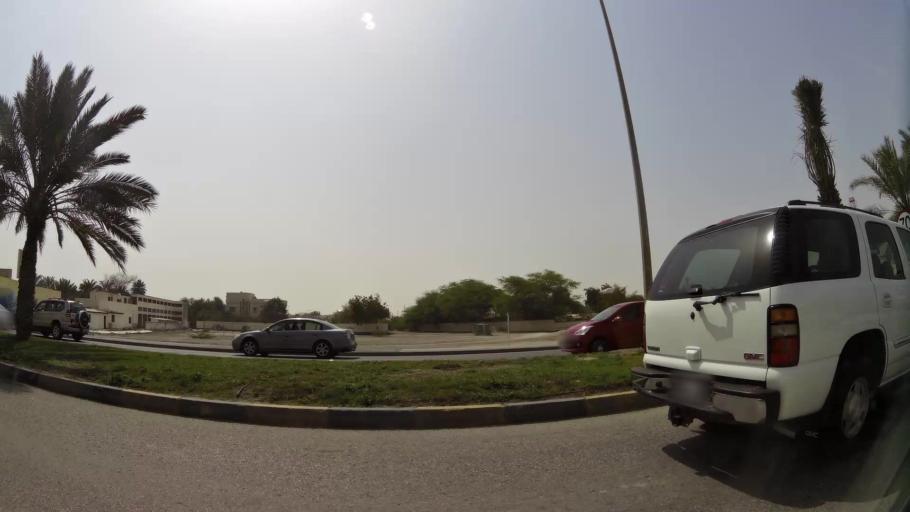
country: BH
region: Manama
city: Jidd Hafs
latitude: 26.2206
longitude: 50.5052
